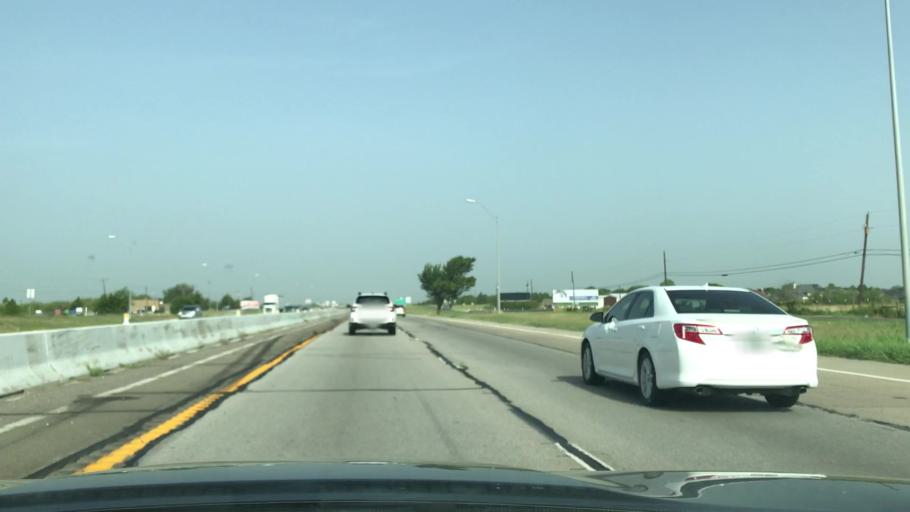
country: US
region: Texas
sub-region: Dallas County
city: Sunnyvale
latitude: 32.7868
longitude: -96.5732
